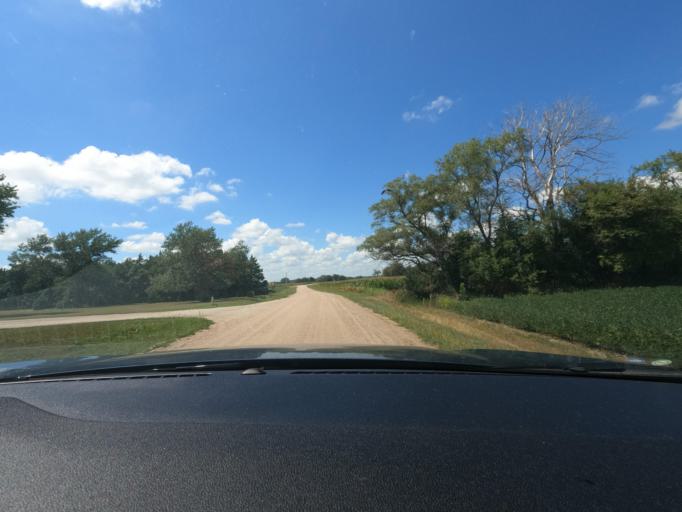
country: US
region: Nebraska
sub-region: Saunders County
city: Wahoo
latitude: 41.2494
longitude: -96.5608
